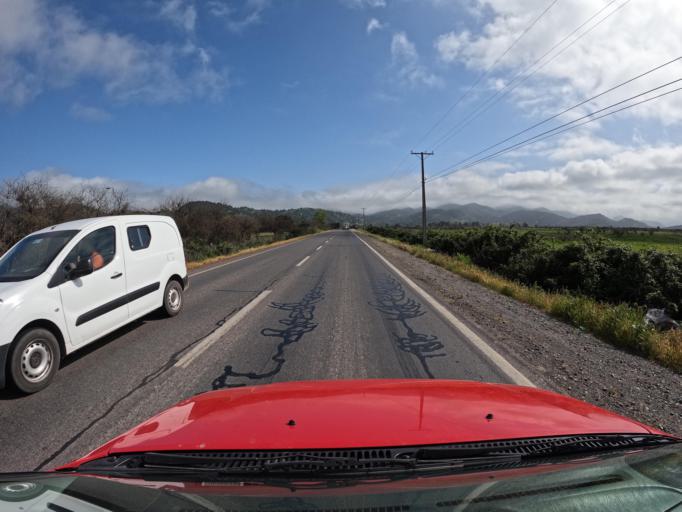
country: CL
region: Maule
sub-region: Provincia de Curico
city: Teno
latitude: -34.8391
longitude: -71.1873
